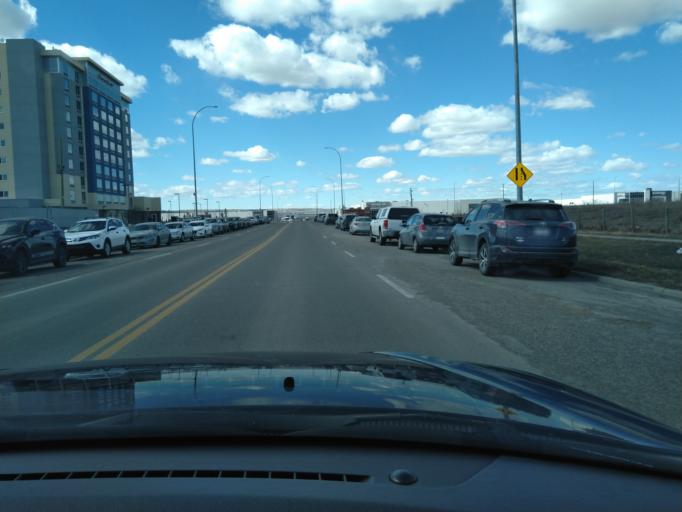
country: CA
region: Alberta
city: Calgary
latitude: 51.1434
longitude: -114.0099
